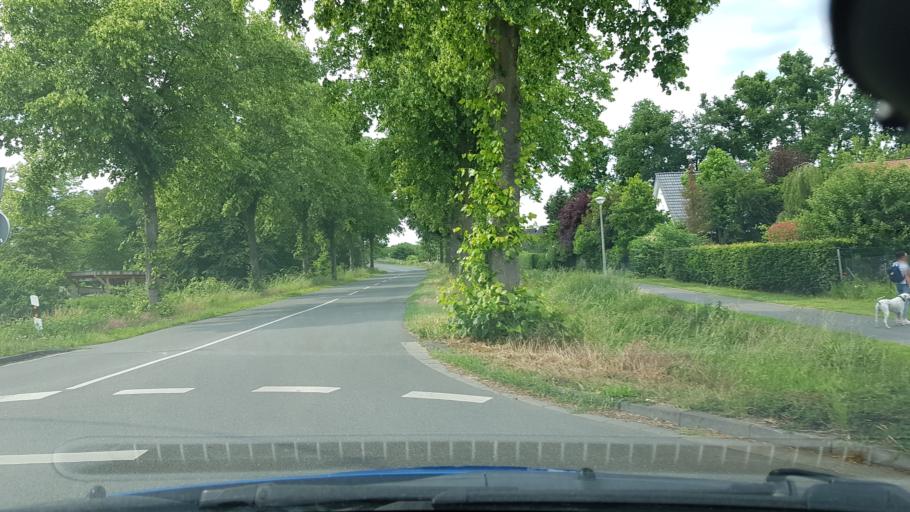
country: DE
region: North Rhine-Westphalia
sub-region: Regierungsbezirk Munster
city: Steinfurt
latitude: 52.1190
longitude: 7.3723
